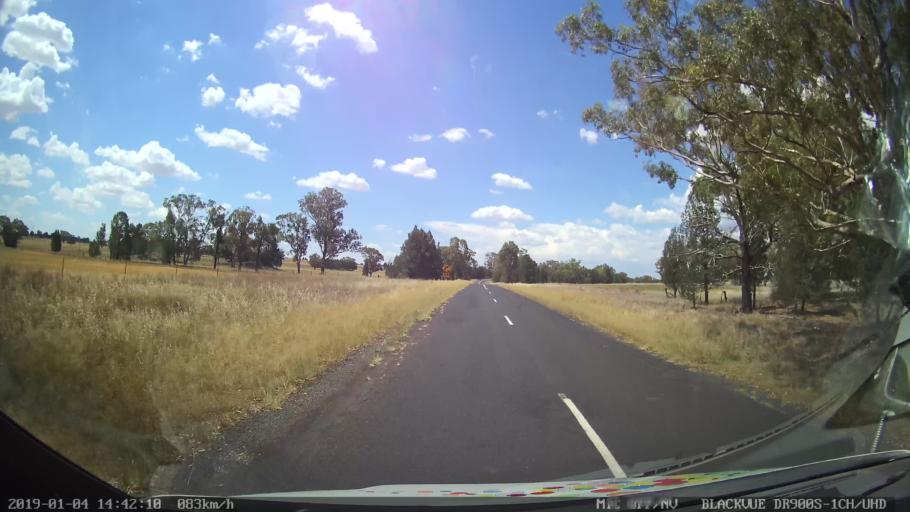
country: AU
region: New South Wales
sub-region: Dubbo Municipality
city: Dubbo
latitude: -32.1312
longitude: 148.6405
